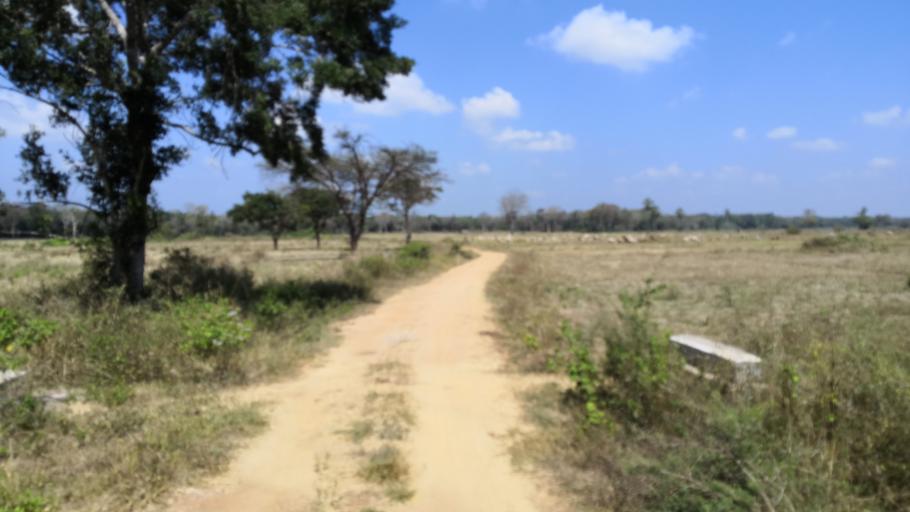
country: LK
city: Padaviya Divisional Secretariat
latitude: 8.9620
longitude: 80.6939
